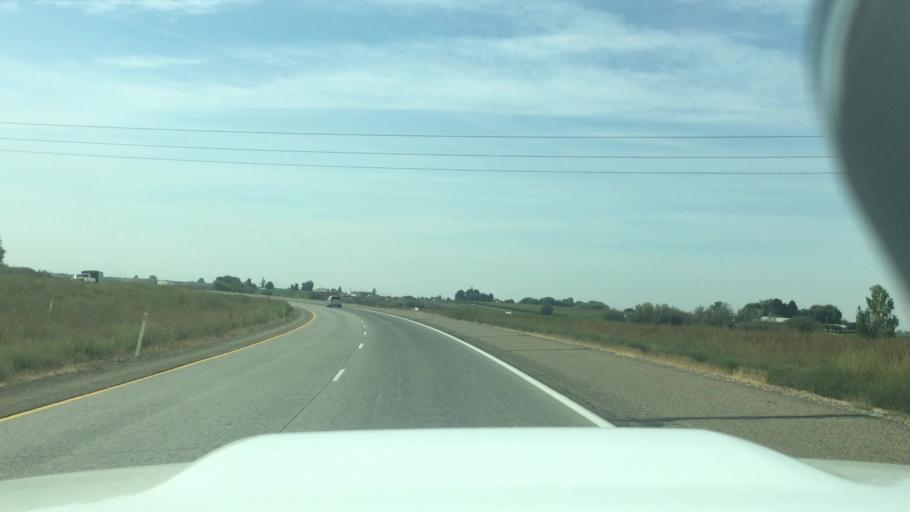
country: US
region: Washington
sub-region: Yakima County
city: Granger
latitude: 46.3378
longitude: -120.1326
